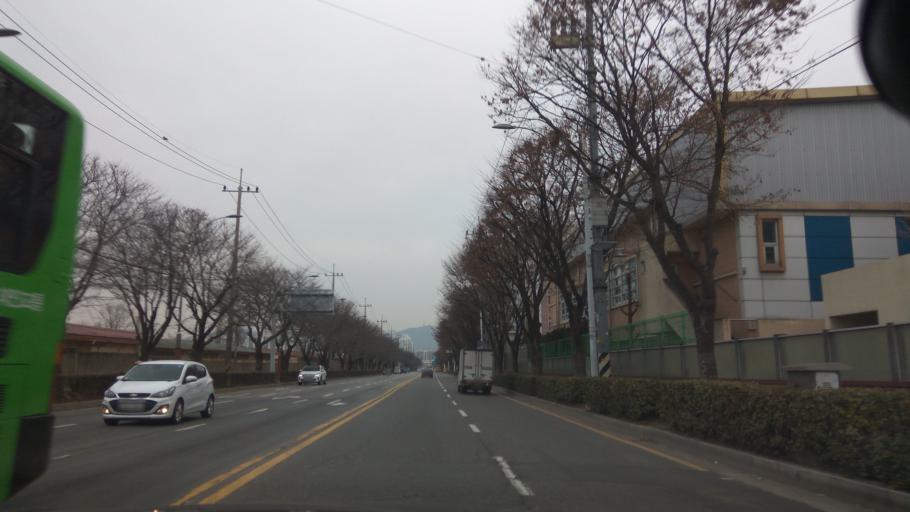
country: KR
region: Incheon
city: Incheon
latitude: 37.4915
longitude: 126.7164
